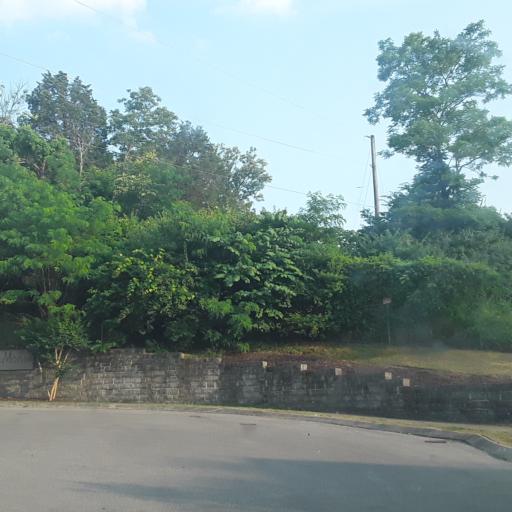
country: US
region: Tennessee
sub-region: Williamson County
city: Brentwood Estates
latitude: 36.0378
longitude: -86.7202
